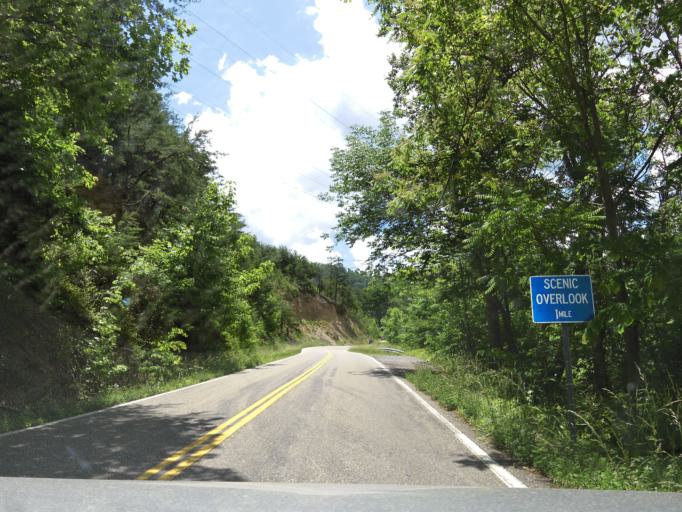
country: US
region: Tennessee
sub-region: Loudon County
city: Greenback
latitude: 35.5096
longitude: -83.9851
